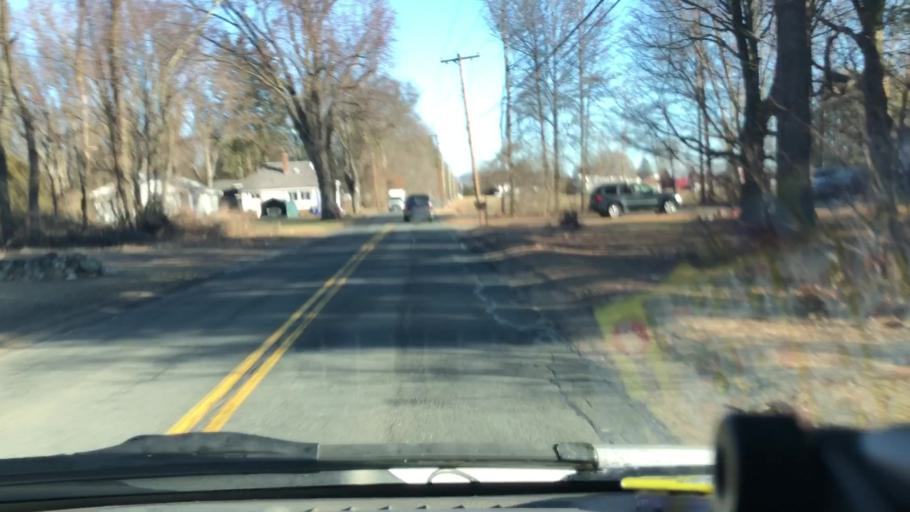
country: US
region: Massachusetts
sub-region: Hampshire County
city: North Amherst
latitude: 42.3915
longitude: -72.5475
